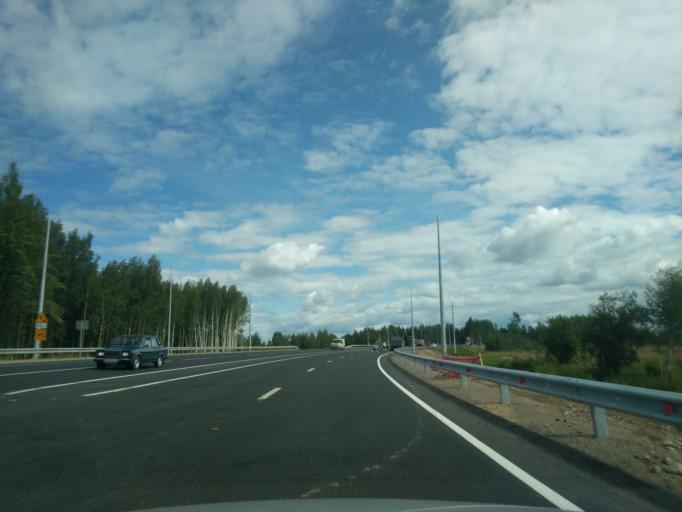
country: RU
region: Kostroma
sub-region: Kostromskoy Rayon
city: Kostroma
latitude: 57.7413
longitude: 40.8545
